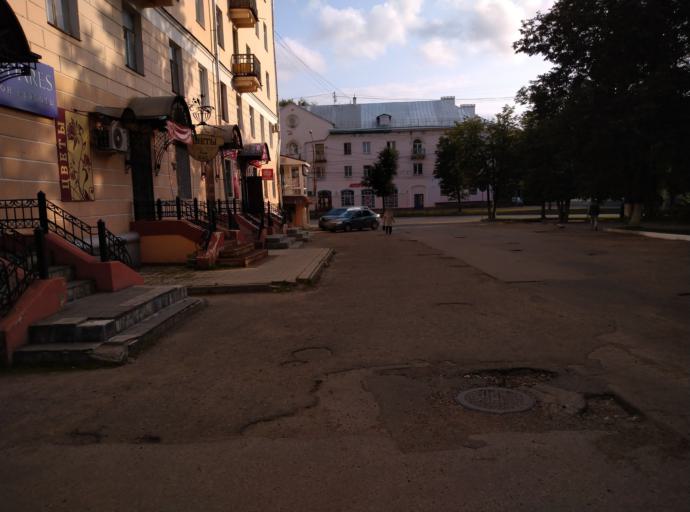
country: RU
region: Kostroma
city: Oktyabr'skiy
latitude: 57.7587
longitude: 40.9718
